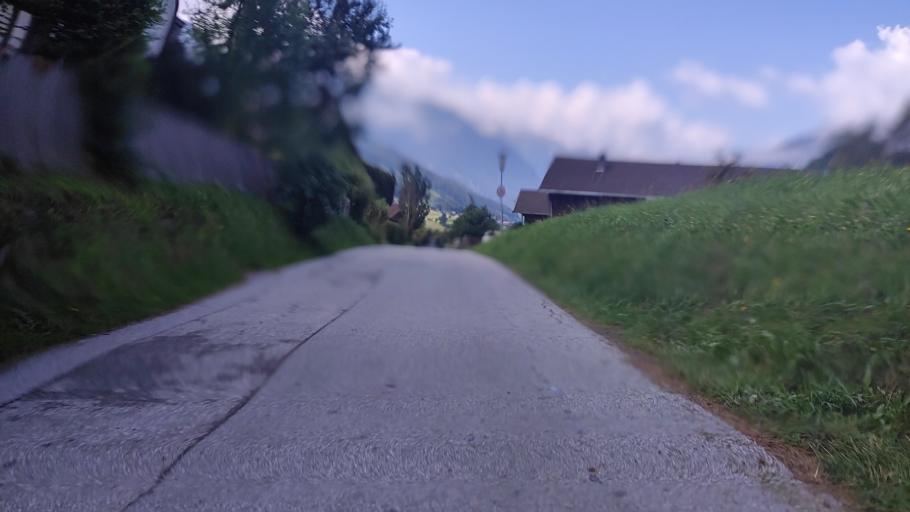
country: AT
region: Salzburg
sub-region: Politischer Bezirk Zell am See
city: Bramberg am Wildkogel
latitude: 47.2796
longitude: 12.3737
